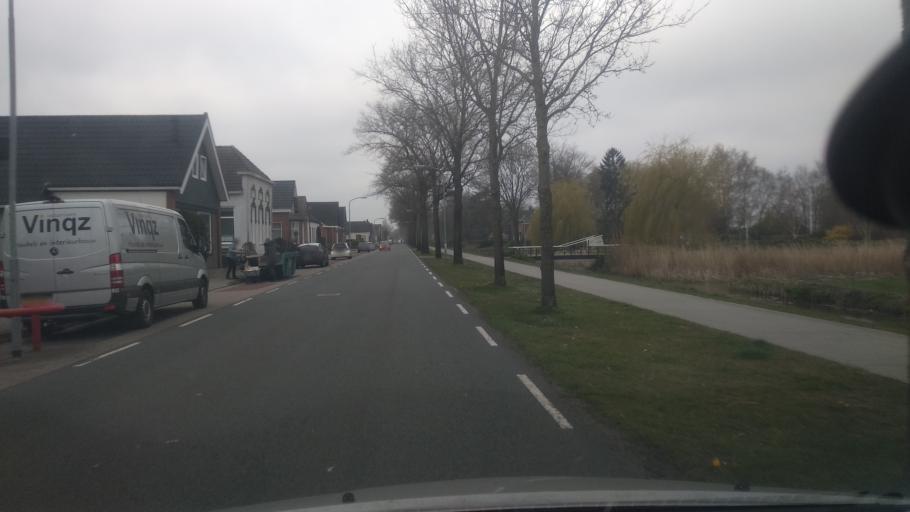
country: NL
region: Groningen
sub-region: Gemeente Stadskanaal
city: Stadskanaal
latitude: 52.9638
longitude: 6.9480
